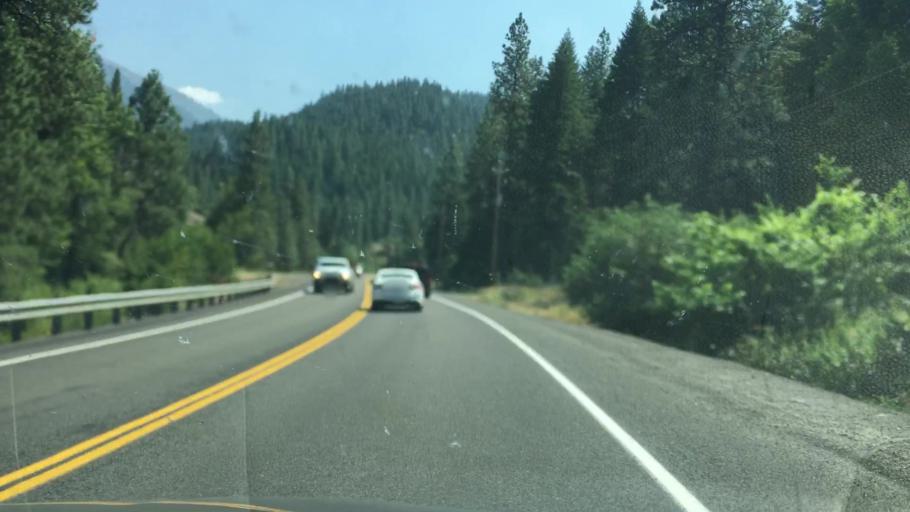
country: US
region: Idaho
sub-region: Valley County
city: McCall
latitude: 45.1874
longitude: -116.3043
